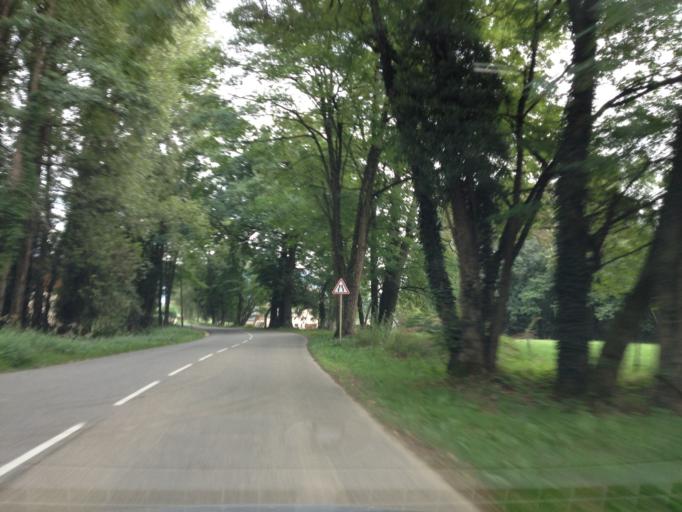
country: FR
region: Rhone-Alpes
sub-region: Departement de la Savoie
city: La Motte-Servolex
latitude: 45.6090
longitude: 5.8941
